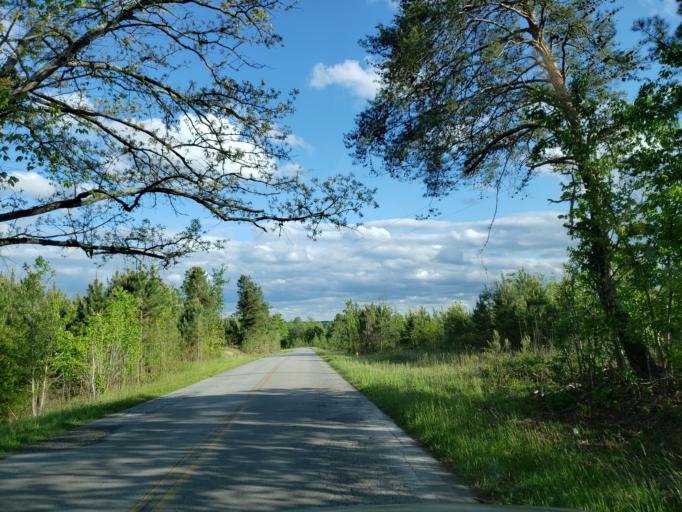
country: US
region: Georgia
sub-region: Haralson County
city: Tallapoosa
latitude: 33.7838
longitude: -85.3204
